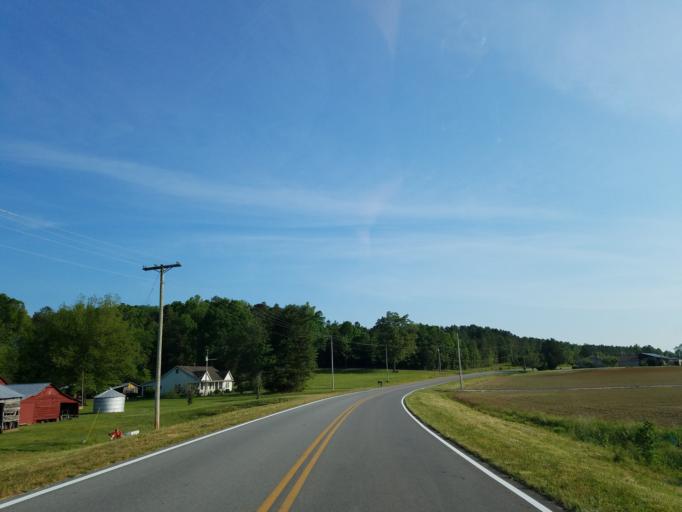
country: US
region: Georgia
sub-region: Chattooga County
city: Trion
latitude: 34.5142
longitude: -85.2309
